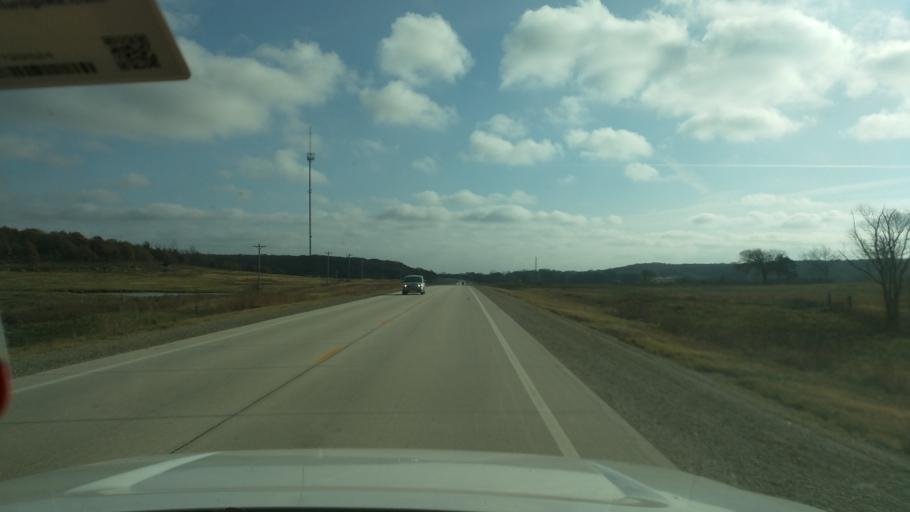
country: US
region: Kansas
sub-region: Montgomery County
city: Caney
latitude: 37.0691
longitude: -96.0346
